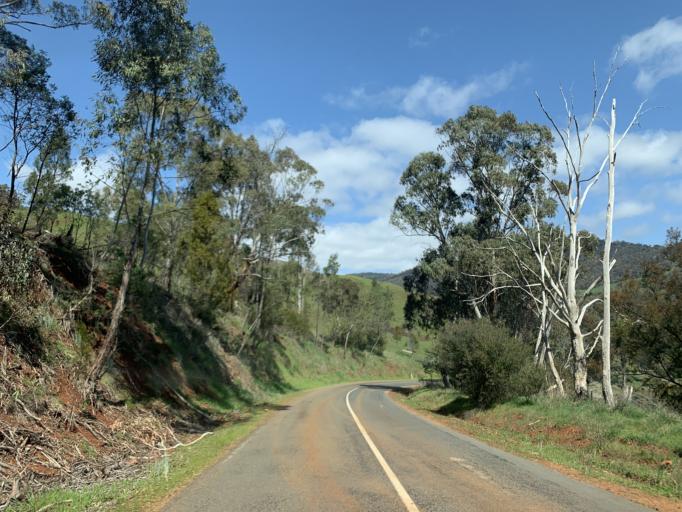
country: AU
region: Victoria
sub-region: Mansfield
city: Mansfield
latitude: -36.8270
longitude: 146.1293
